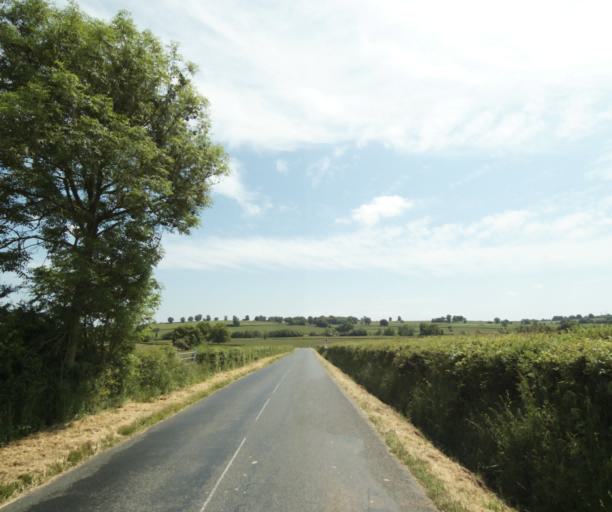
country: FR
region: Bourgogne
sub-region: Departement de Saone-et-Loire
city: Palinges
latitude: 46.5700
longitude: 4.1545
